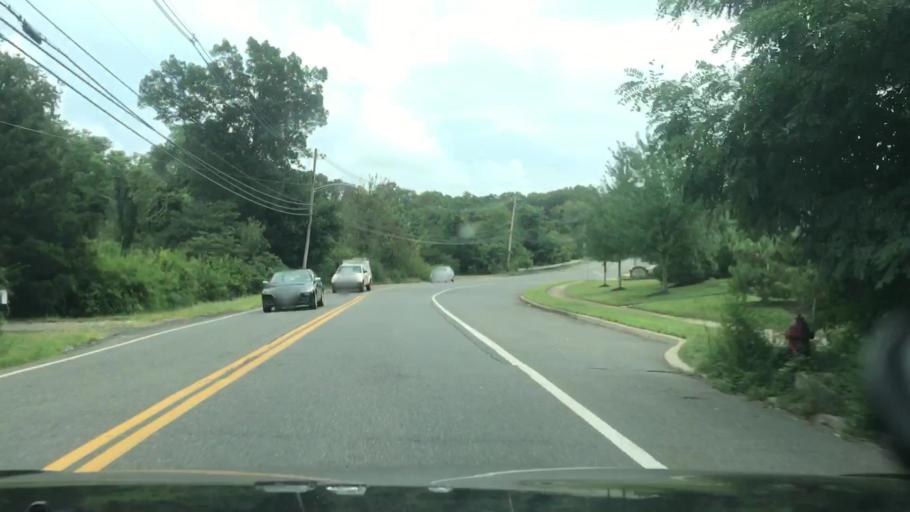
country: US
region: New Jersey
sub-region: Ocean County
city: Barnegat
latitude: 39.7547
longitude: -74.2381
